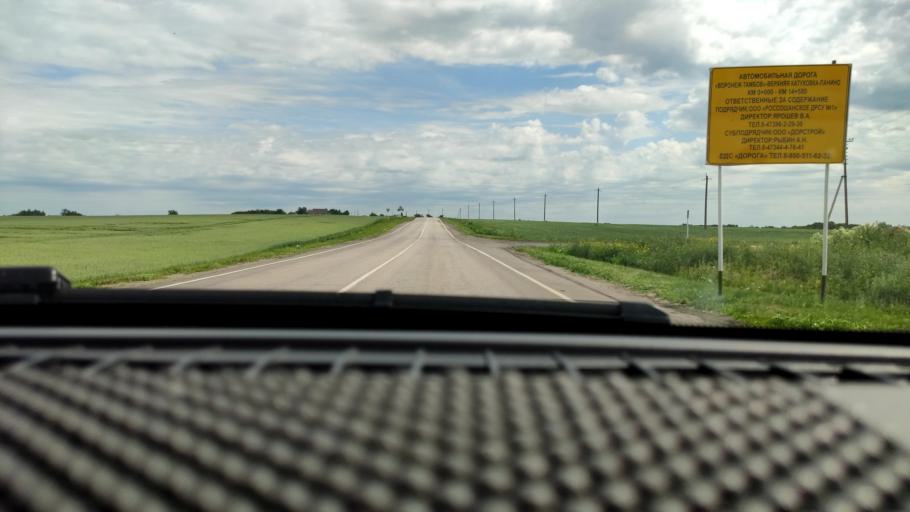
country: RU
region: Voronezj
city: Verkhnyaya Khava
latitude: 51.6875
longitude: 39.9320
